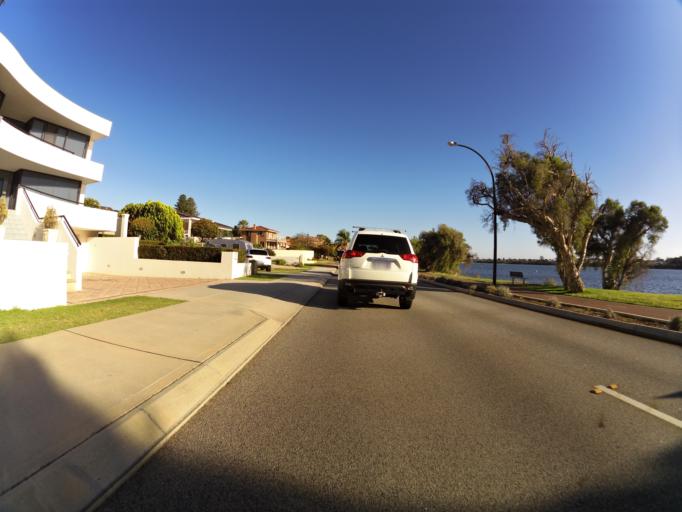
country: AU
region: Western Australia
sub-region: Melville
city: Mount Pleasant
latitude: -32.0314
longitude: 115.8530
